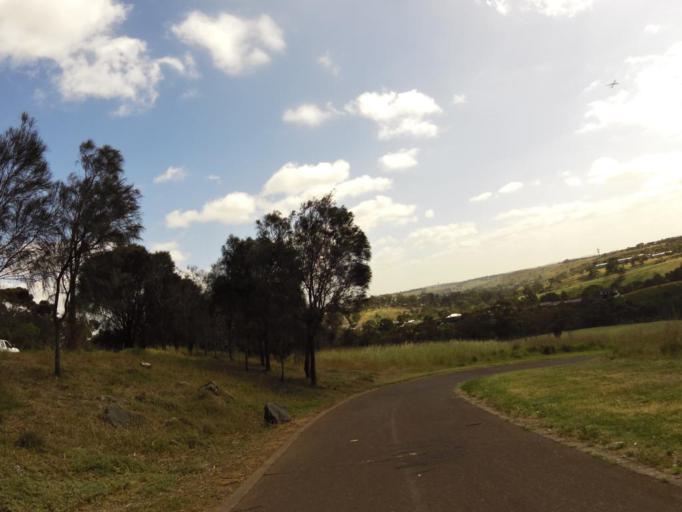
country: AU
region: Victoria
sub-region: Brimbank
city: Kealba
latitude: -37.7323
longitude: 144.8402
